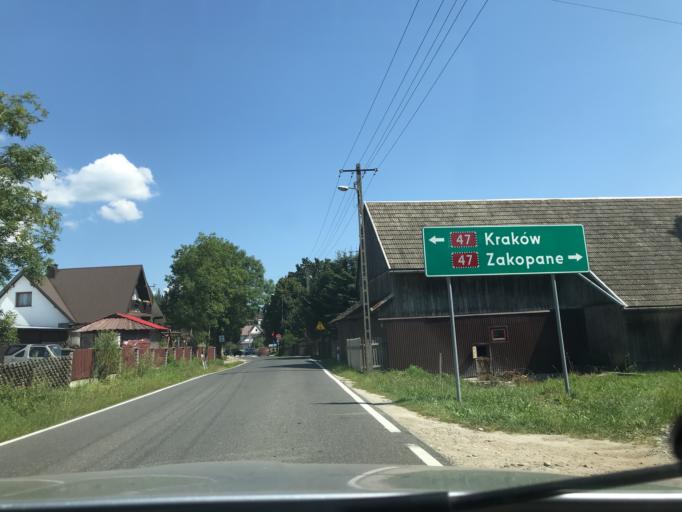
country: PL
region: Lesser Poland Voivodeship
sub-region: Powiat nowotarski
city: Klikuszowa
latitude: 49.5194
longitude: 19.9832
